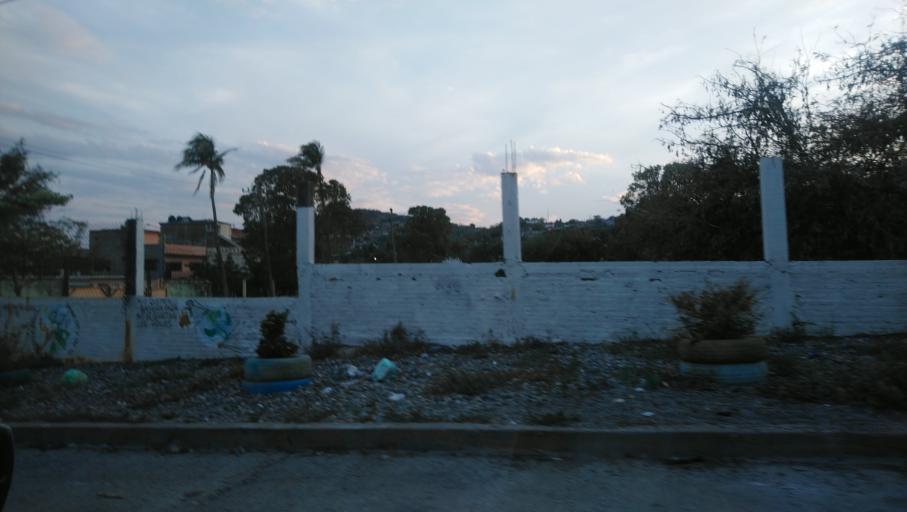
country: MX
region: Oaxaca
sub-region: Salina Cruz
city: Salina Cruz
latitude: 16.1854
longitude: -95.1977
